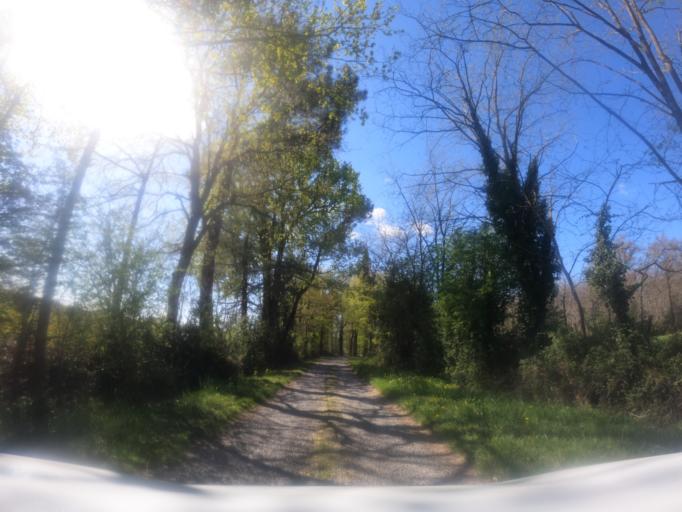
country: FR
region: Pays de la Loire
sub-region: Departement de la Vendee
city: Saint-Vincent-sur-Graon
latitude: 46.5185
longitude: -1.3684
